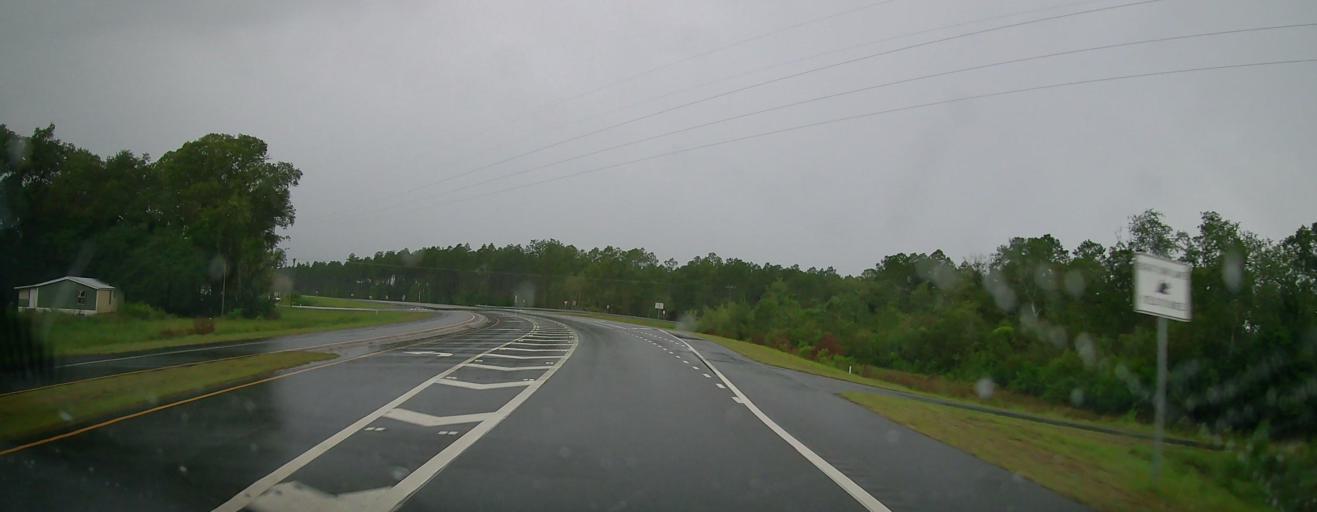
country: US
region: Georgia
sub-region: Clinch County
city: Homerville
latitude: 31.0766
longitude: -82.6477
